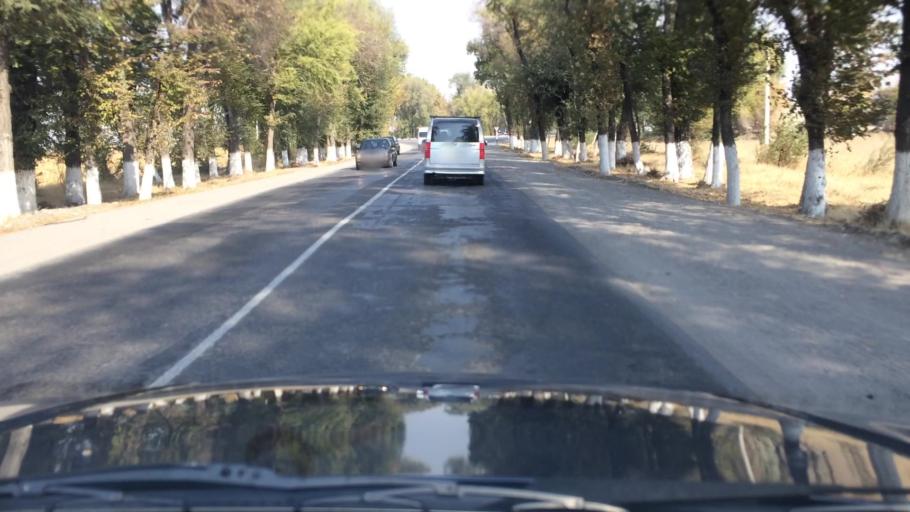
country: KG
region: Chuy
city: Lebedinovka
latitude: 42.9288
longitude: 74.6910
